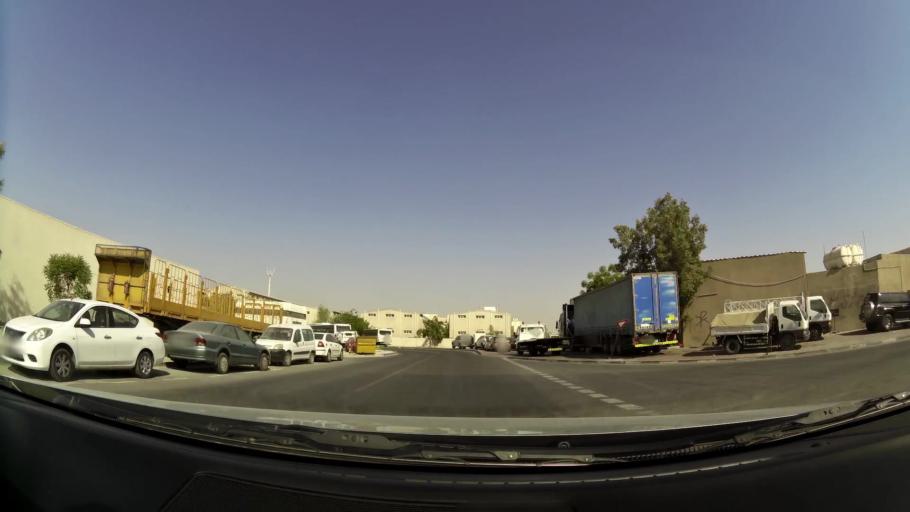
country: AE
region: Dubai
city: Dubai
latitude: 25.1247
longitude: 55.2258
